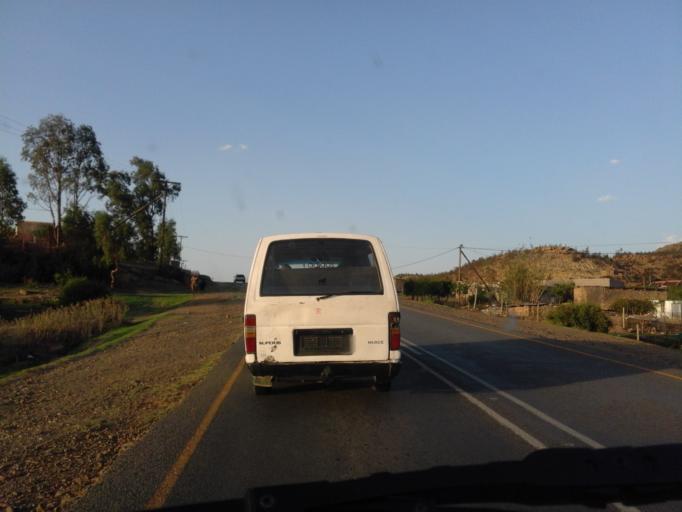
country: LS
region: Mafeteng
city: Mafeteng
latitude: -29.8385
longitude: 27.2328
